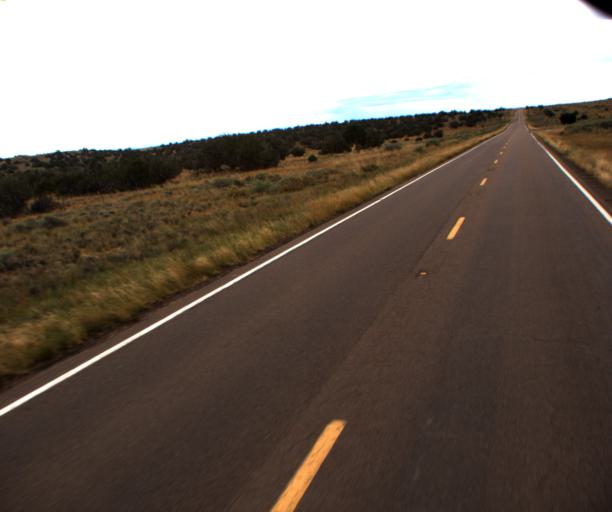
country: US
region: Arizona
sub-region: Navajo County
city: Snowflake
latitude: 34.6167
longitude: -110.0914
